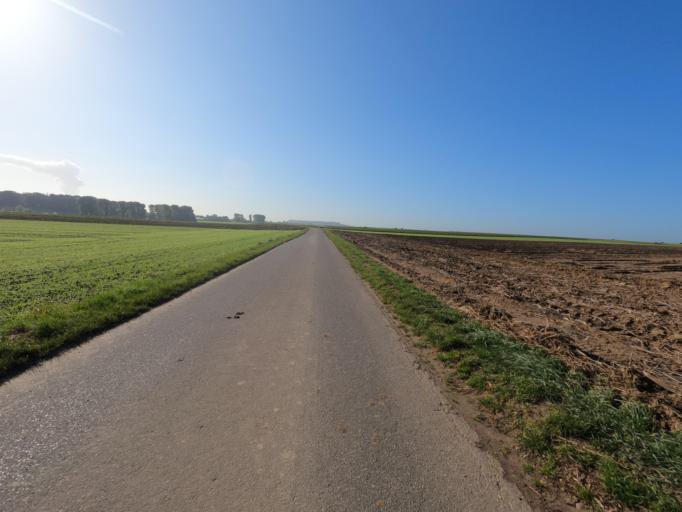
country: DE
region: North Rhine-Westphalia
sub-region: Regierungsbezirk Koln
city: Linnich
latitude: 50.9733
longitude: 6.2547
